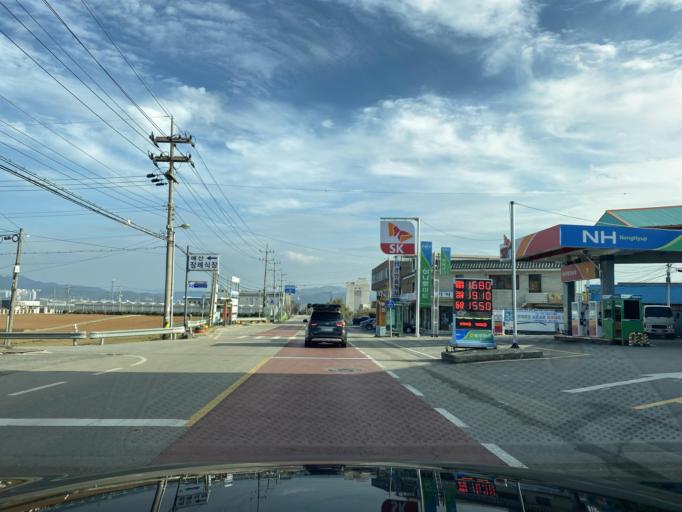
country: KR
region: Chungcheongnam-do
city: Yesan
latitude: 36.6876
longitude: 126.7985
